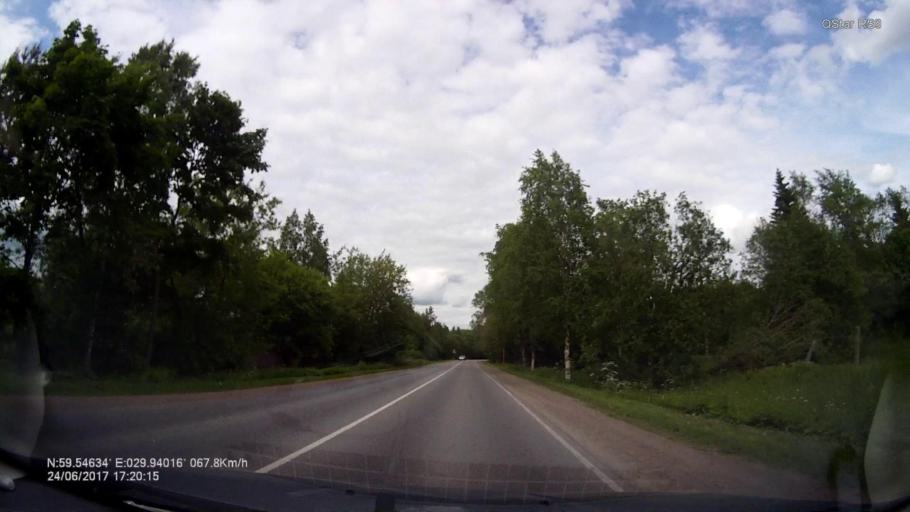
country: RU
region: Leningrad
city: Voyskovitsy
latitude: 59.5466
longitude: 29.9409
